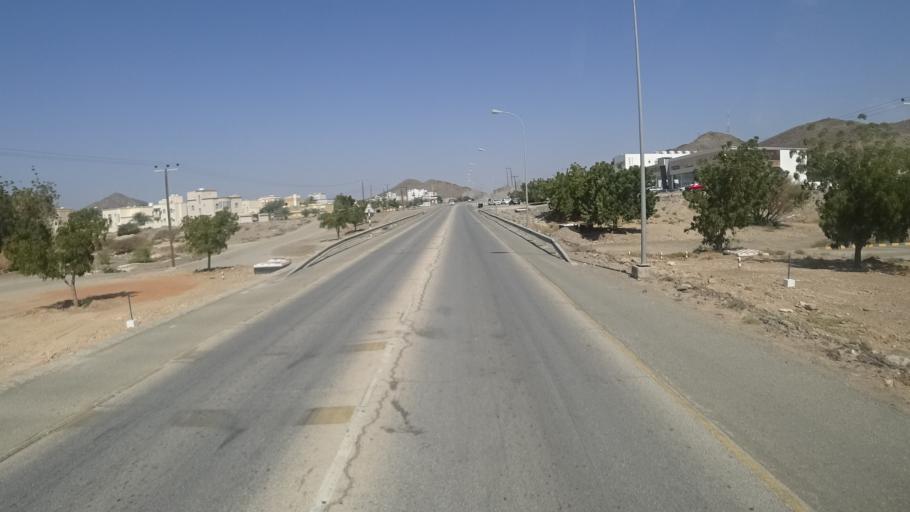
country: OM
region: Ash Sharqiyah
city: Ibra'
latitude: 22.6896
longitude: 58.5515
